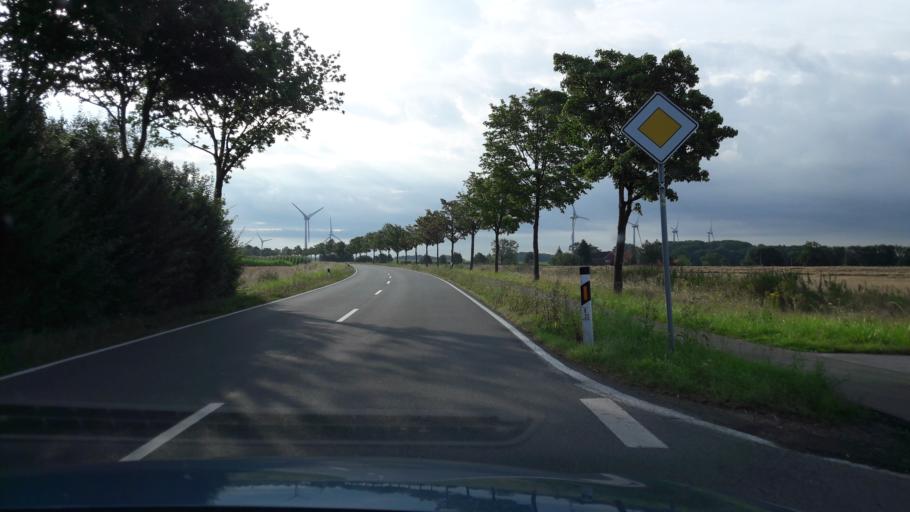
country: DE
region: North Rhine-Westphalia
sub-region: Regierungsbezirk Munster
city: Ennigerloh
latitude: 51.8636
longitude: 7.9544
